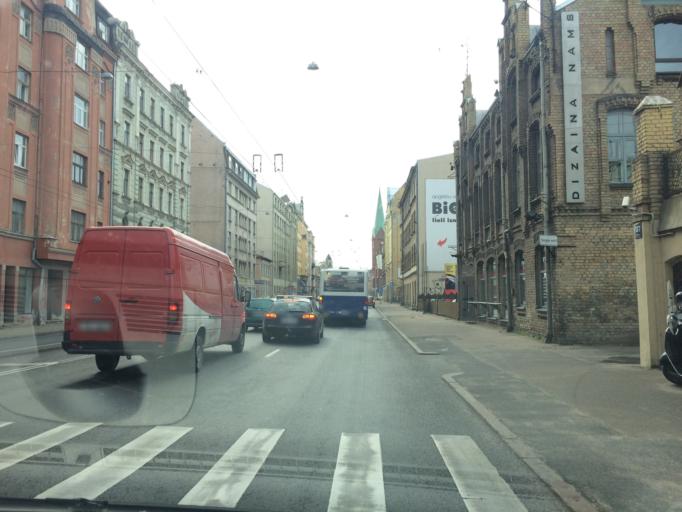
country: LV
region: Riga
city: Riga
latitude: 56.9646
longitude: 24.1408
